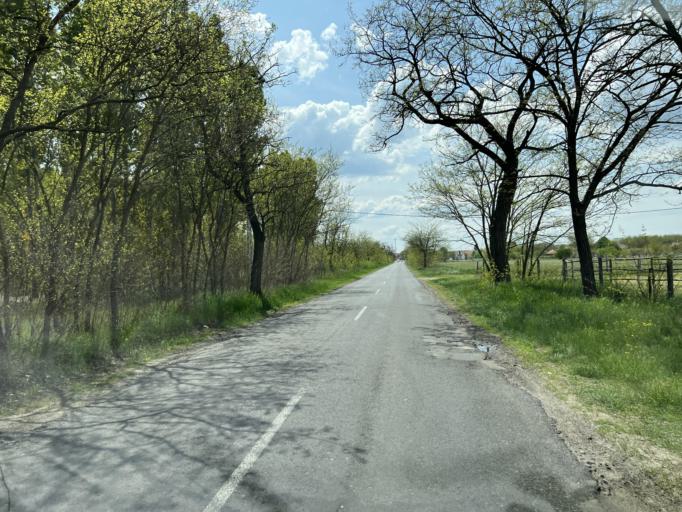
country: HU
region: Pest
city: Csemo
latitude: 47.1227
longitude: 19.7027
